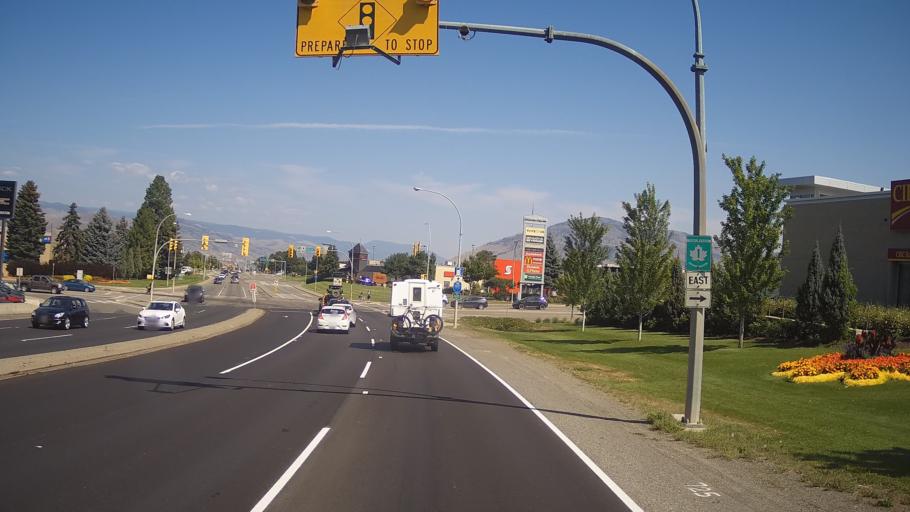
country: CA
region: British Columbia
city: Kamloops
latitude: 50.6628
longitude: -120.3539
